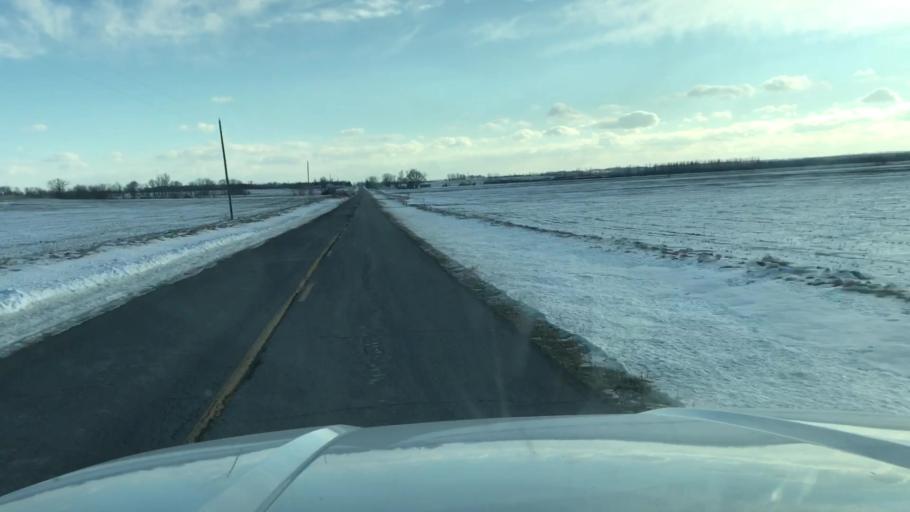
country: US
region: Missouri
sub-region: Holt County
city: Oregon
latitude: 40.1261
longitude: -95.0224
